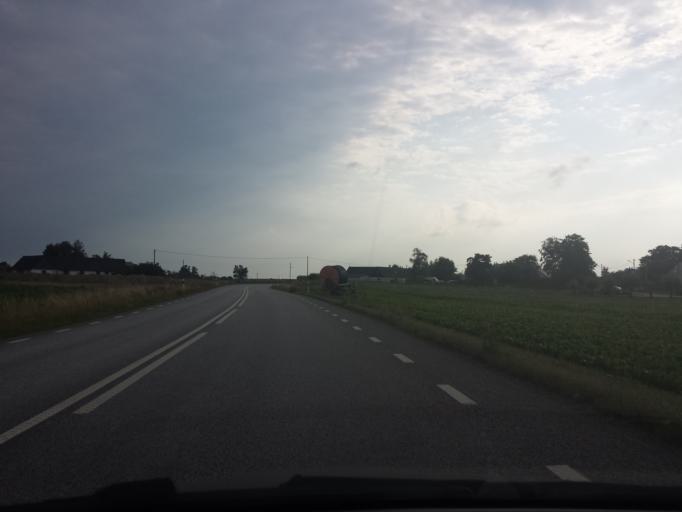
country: SE
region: Skane
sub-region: Ystads Kommun
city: Kopingebro
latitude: 55.4367
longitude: 13.9813
